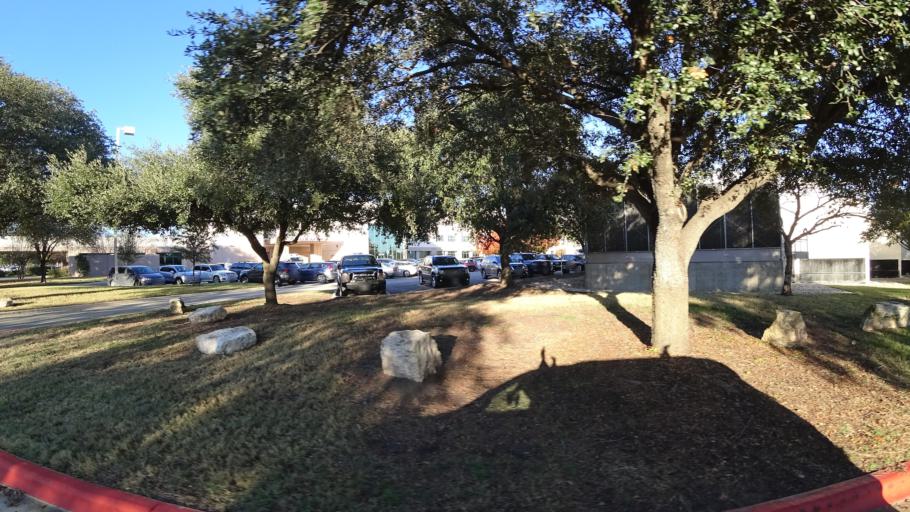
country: US
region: Texas
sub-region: Travis County
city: Wells Branch
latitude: 30.4101
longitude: -97.7069
